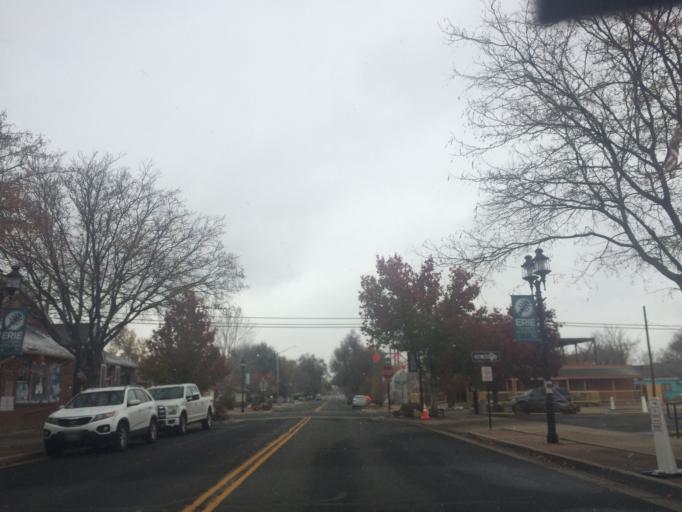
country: US
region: Colorado
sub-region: Boulder County
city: Erie
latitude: 40.0498
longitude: -105.0474
